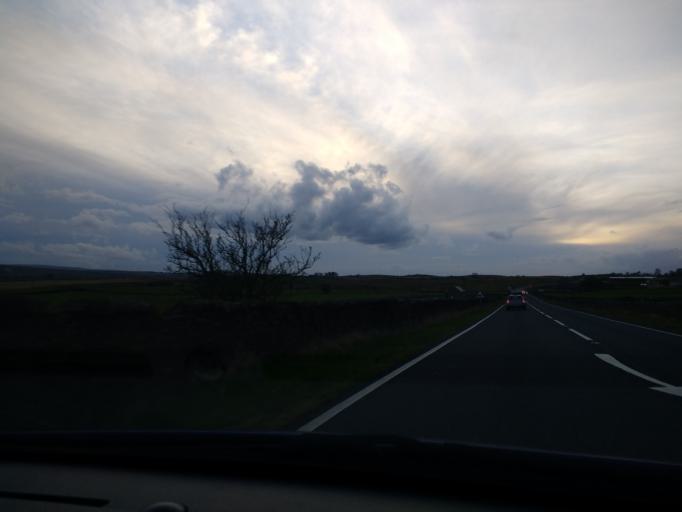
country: GB
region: England
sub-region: North Yorkshire
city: Ingleton
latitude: 54.1235
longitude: -2.4150
